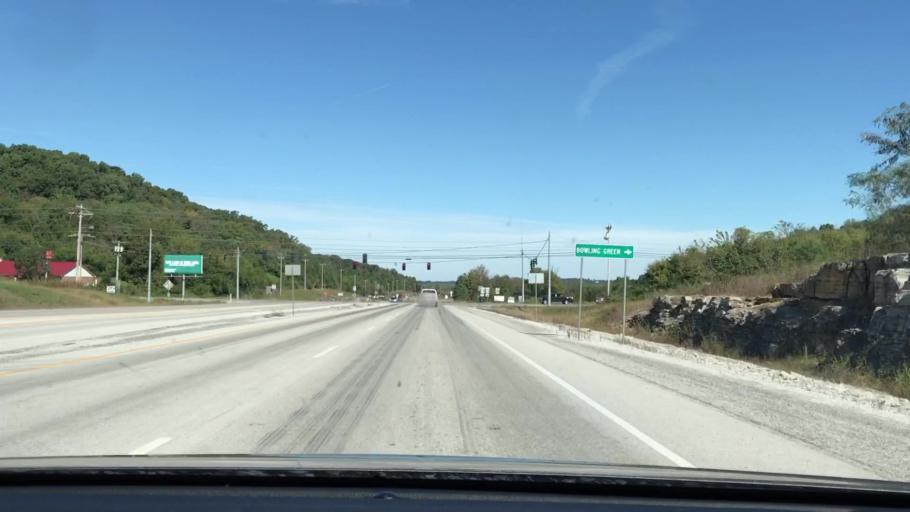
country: US
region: Kentucky
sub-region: Logan County
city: Russellville
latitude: 36.8409
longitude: -86.8635
